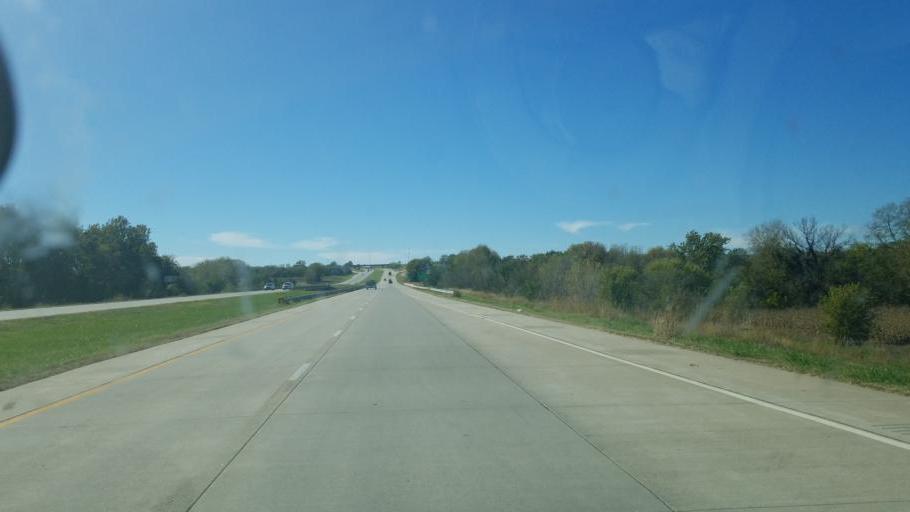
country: US
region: Kansas
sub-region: Riley County
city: Ogden
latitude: 39.0615
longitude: -96.7278
